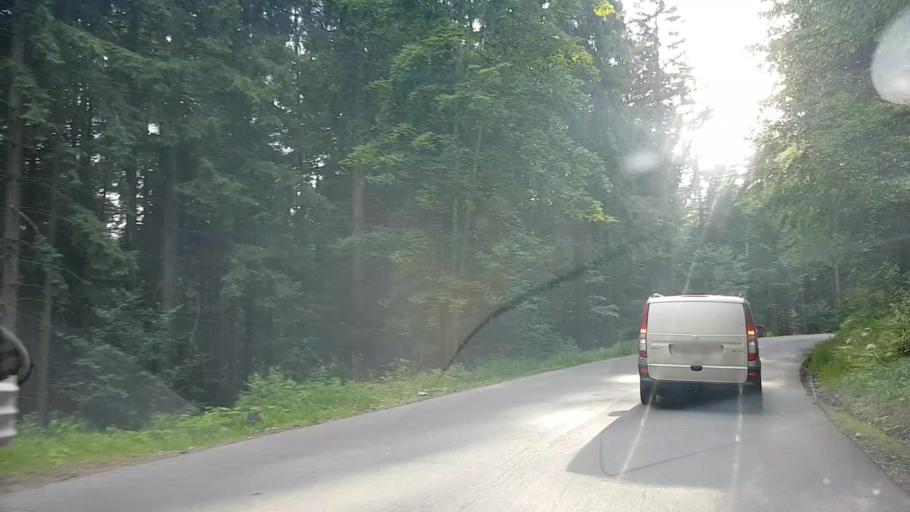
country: RO
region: Harghita
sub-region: Comuna Varsag
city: Varsag
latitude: 46.6689
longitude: 25.3318
